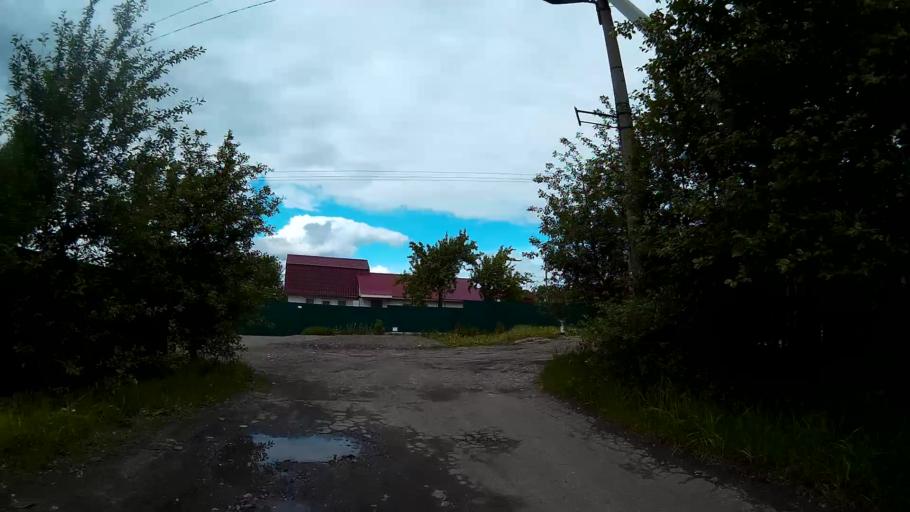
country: RU
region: Ulyanovsk
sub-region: Ulyanovskiy Rayon
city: Ulyanovsk
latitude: 54.2599
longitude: 48.3099
